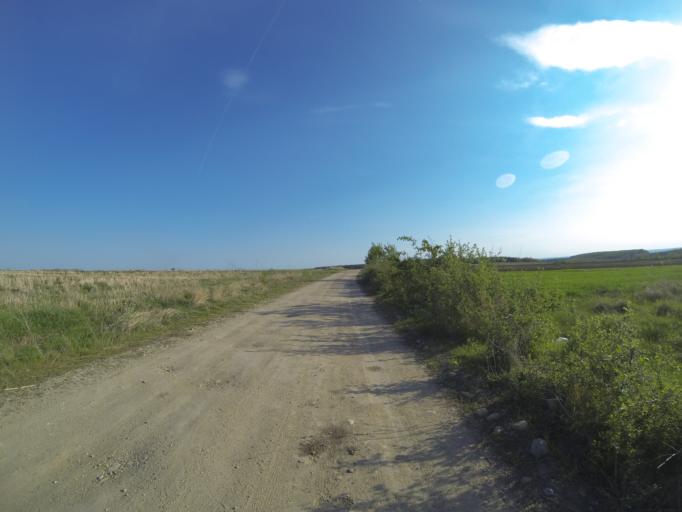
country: RO
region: Dolj
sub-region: Comuna Filiasi
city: Fratostita
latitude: 44.5666
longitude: 23.5879
